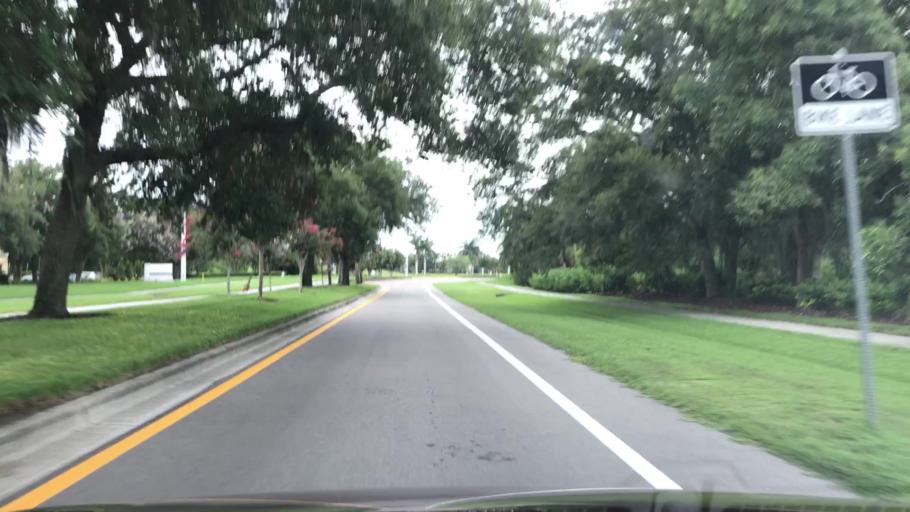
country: US
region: Florida
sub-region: Sarasota County
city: Vamo
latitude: 27.2457
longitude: -82.4680
